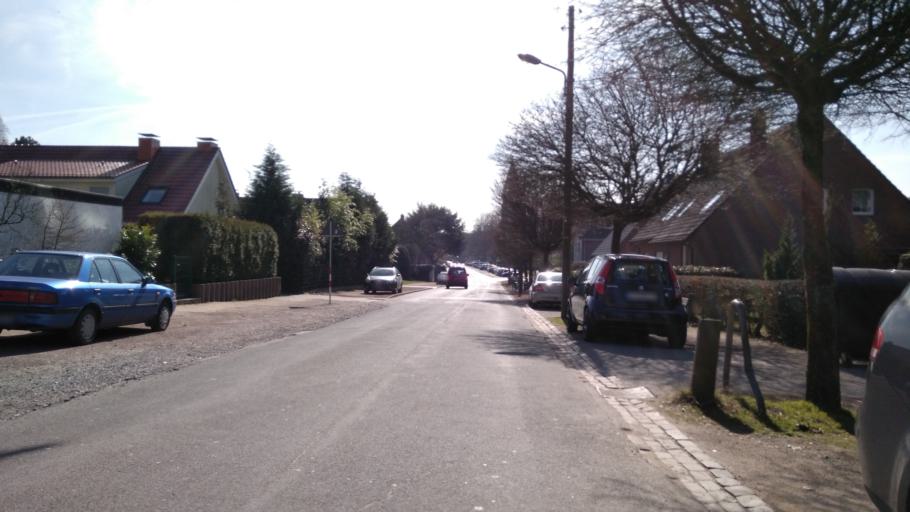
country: DE
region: North Rhine-Westphalia
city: Dorsten
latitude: 51.6063
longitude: 6.9176
